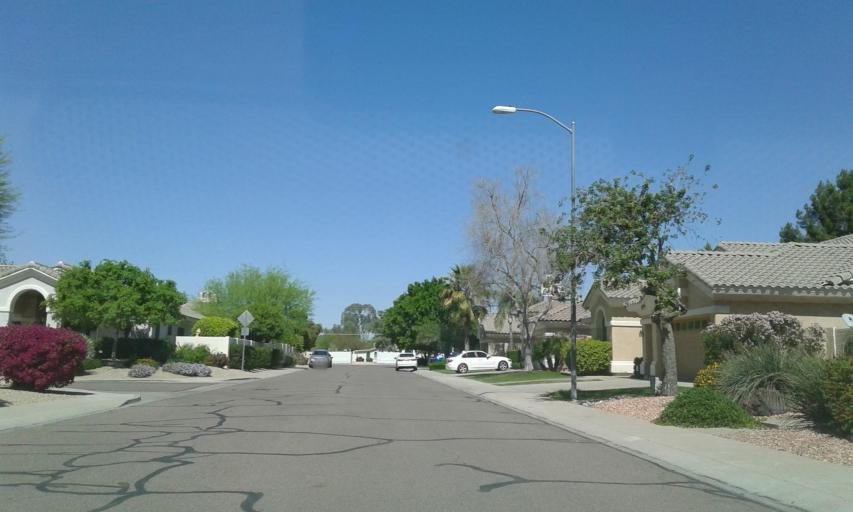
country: US
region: Arizona
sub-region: Maricopa County
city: Paradise Valley
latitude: 33.5814
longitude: -111.9621
